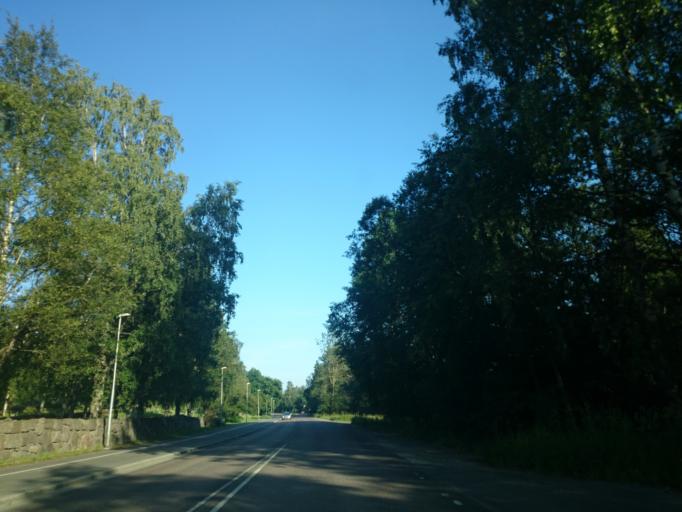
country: SE
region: Vaesternorrland
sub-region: Sundsvalls Kommun
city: Sundsvall
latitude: 62.3963
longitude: 17.2689
